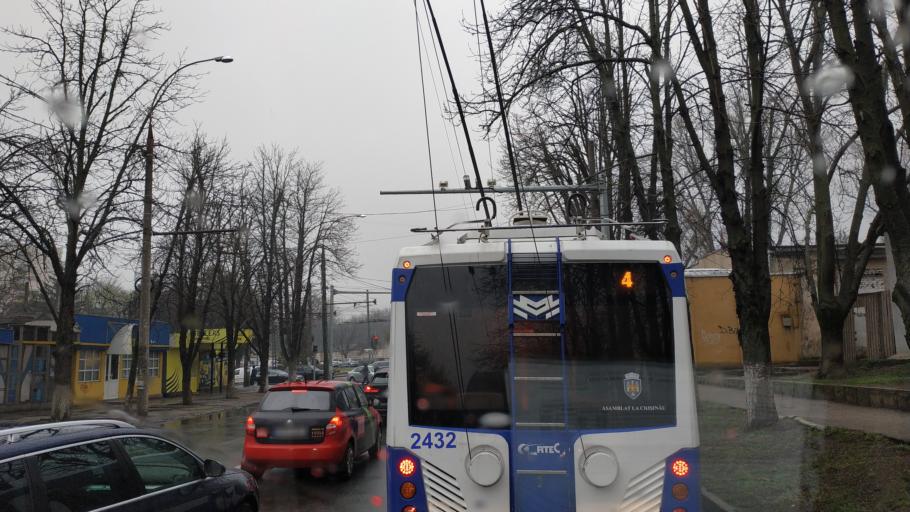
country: MD
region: Chisinau
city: Chisinau
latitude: 47.0224
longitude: 28.8037
